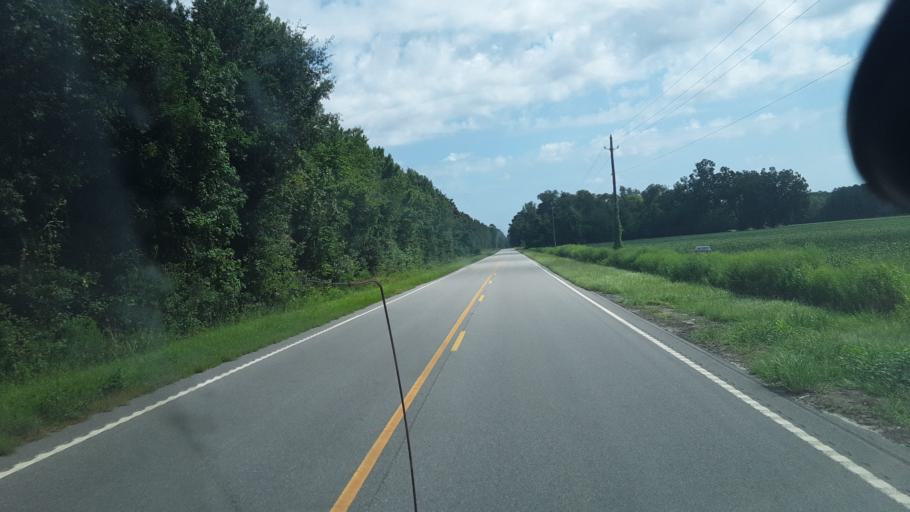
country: US
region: South Carolina
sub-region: Bamberg County
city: Bamberg
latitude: 33.0769
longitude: -81.0250
